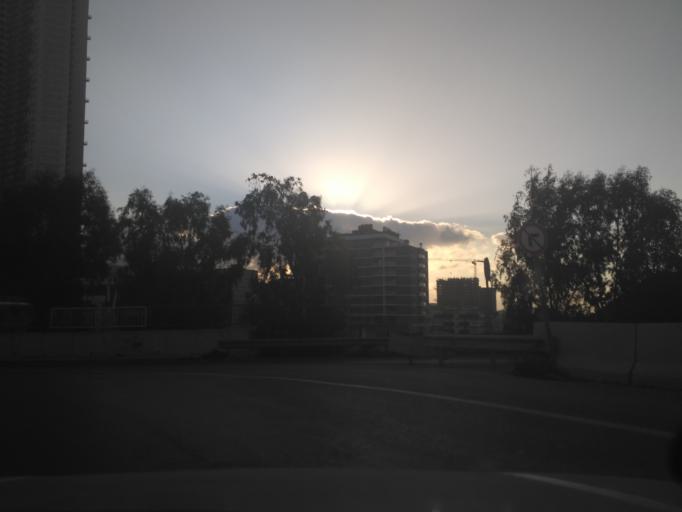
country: TR
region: Izmir
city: Bornova
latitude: 38.4331
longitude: 27.2116
